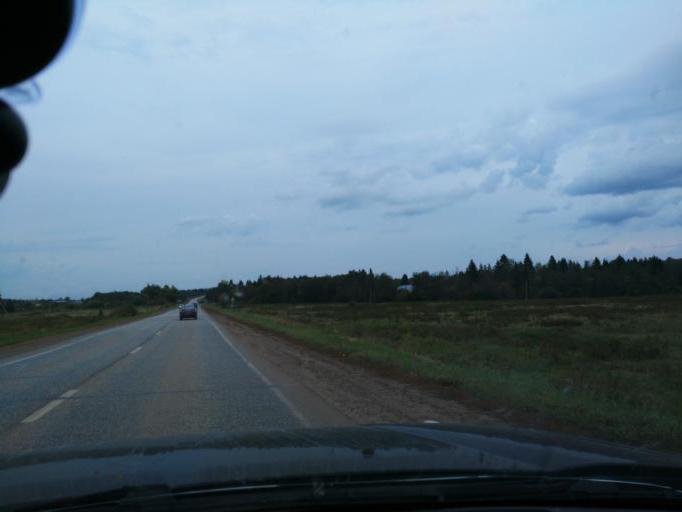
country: RU
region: Perm
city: Chernushka
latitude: 56.5169
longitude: 56.0140
